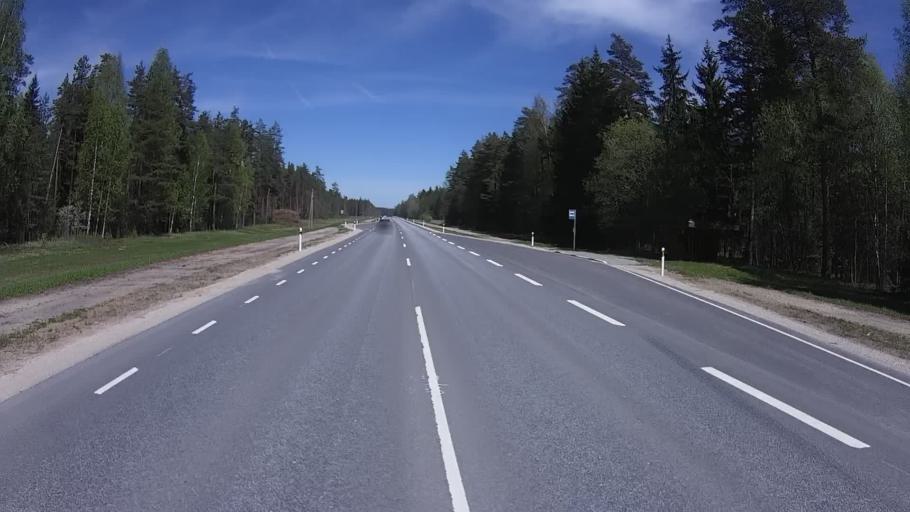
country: EE
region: Vorumaa
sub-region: Voru linn
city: Voru
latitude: 57.7972
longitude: 26.9579
